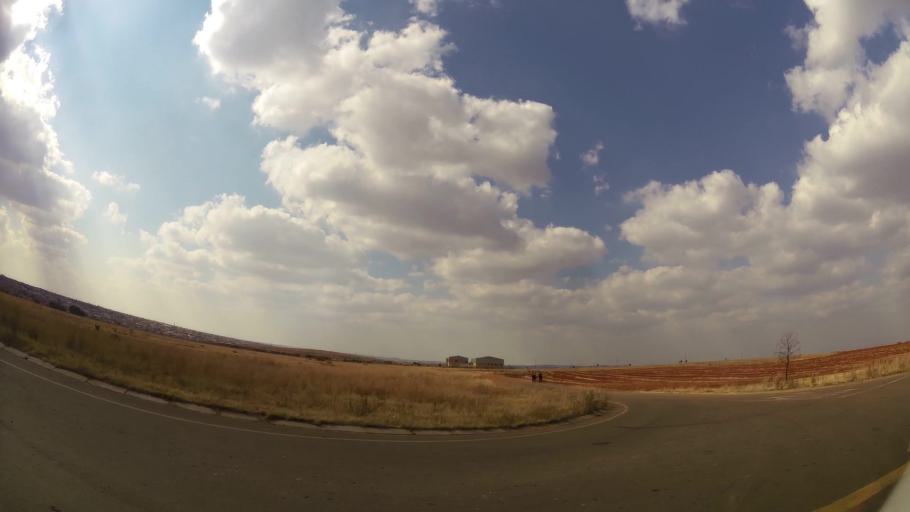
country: ZA
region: Mpumalanga
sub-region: Nkangala District Municipality
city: Delmas
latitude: -26.1142
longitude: 28.6800
